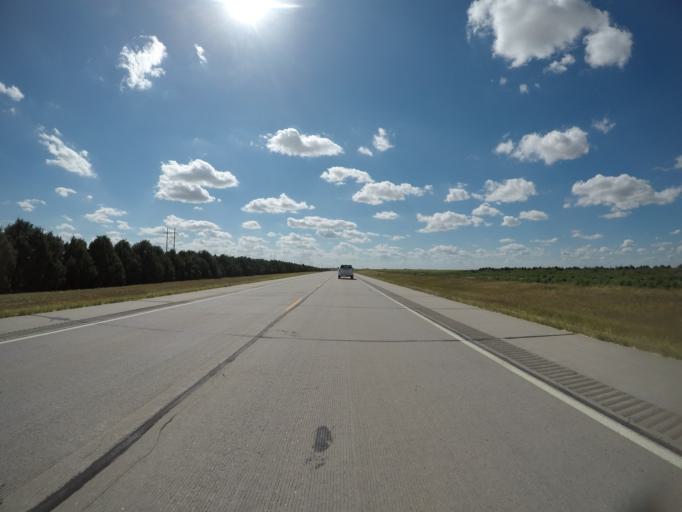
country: US
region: Colorado
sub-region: Phillips County
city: Holyoke
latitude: 40.5988
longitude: -102.3904
